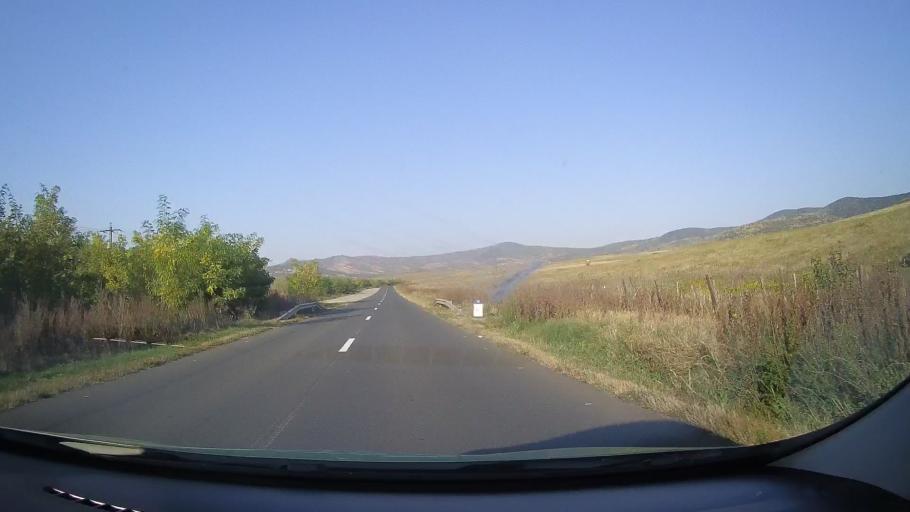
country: RO
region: Arad
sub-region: Comuna Covasint
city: Covasint
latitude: 46.2247
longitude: 21.6306
